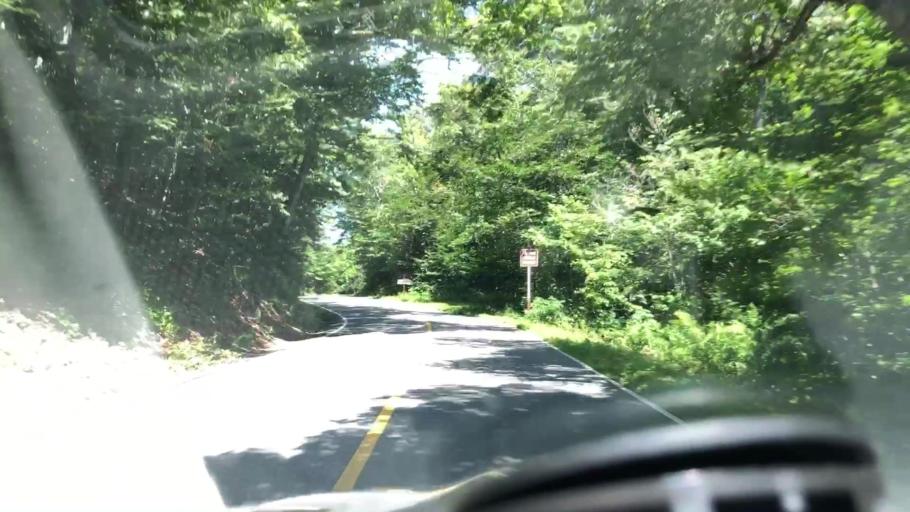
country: US
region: Massachusetts
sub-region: Berkshire County
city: Lanesborough
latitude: 42.5916
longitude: -73.1967
